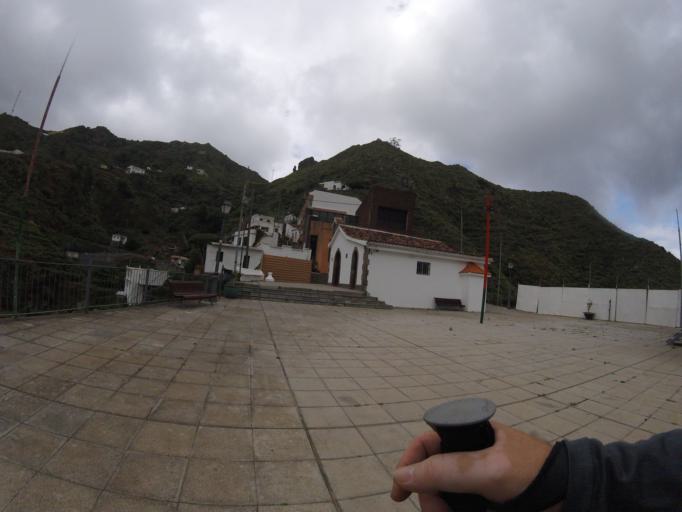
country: ES
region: Canary Islands
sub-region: Provincia de Santa Cruz de Tenerife
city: Tegueste
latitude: 28.5480
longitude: -16.2958
